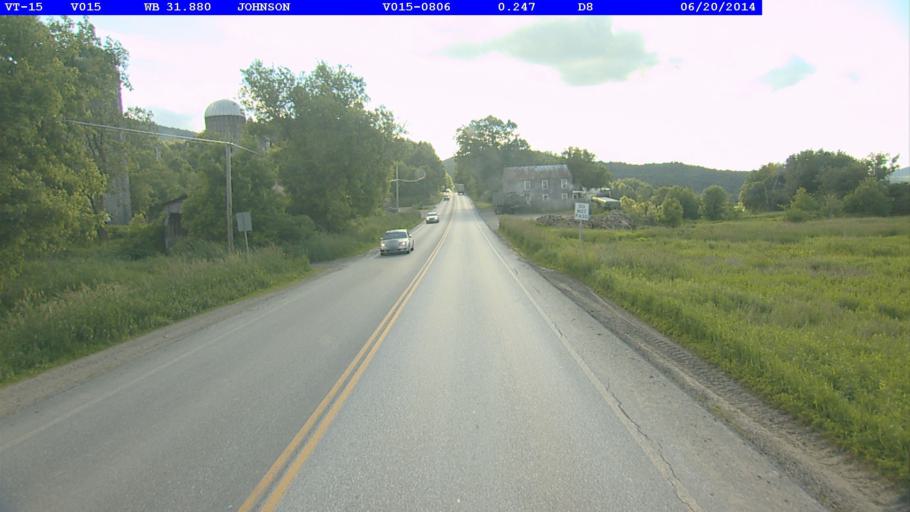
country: US
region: Vermont
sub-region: Lamoille County
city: Johnson
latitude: 44.6500
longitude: -72.7497
